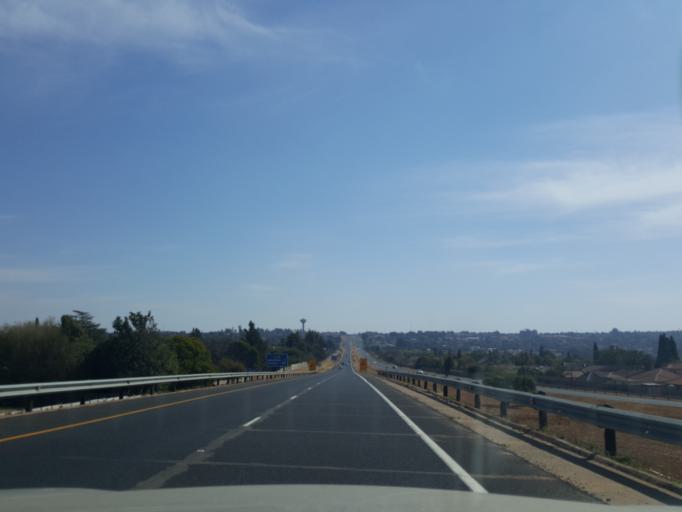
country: ZA
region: Mpumalanga
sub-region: Nkangala District Municipality
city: Witbank
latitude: -25.8964
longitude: 29.2525
